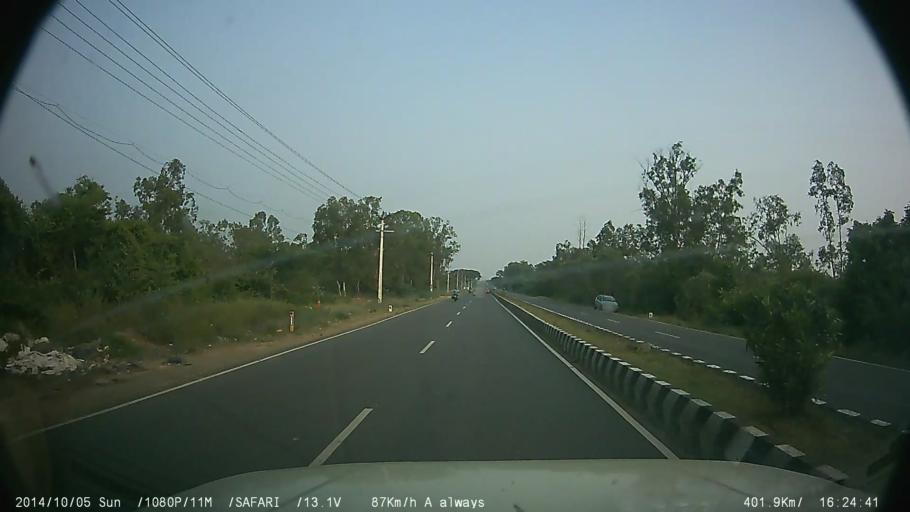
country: IN
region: Tamil Nadu
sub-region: Kancheepuram
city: Vengavasal
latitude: 12.8208
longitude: 80.1726
